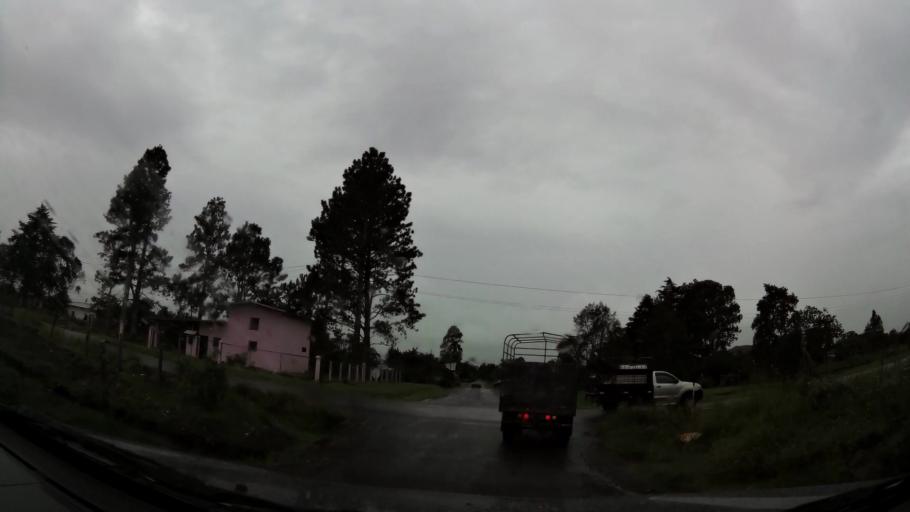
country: PA
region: Chiriqui
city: Volcan
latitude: 8.7891
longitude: -82.6493
